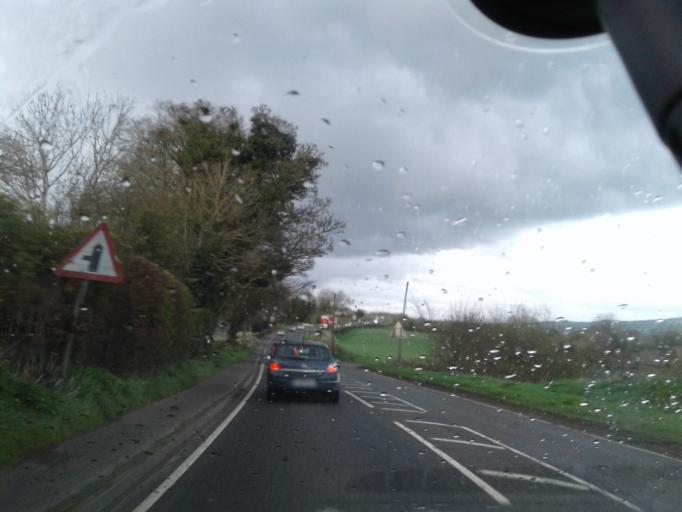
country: GB
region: Northern Ireland
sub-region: Strabane District
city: Sion Mills
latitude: 54.7976
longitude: -7.4755
